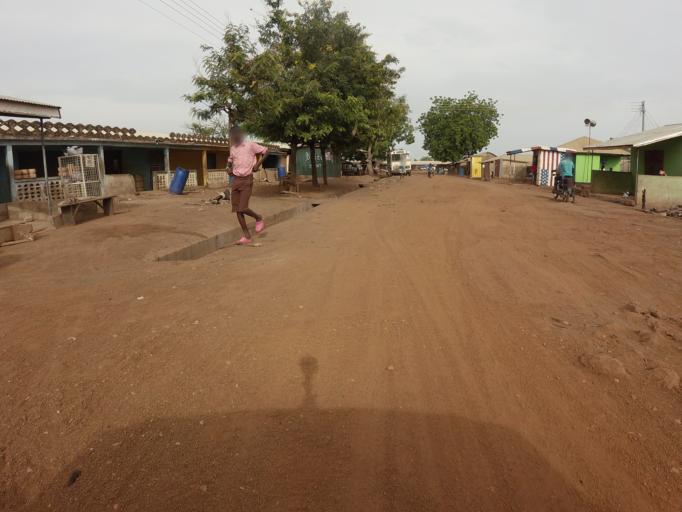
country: GH
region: Northern
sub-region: Yendi
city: Yendi
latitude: 9.9232
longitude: -0.2165
